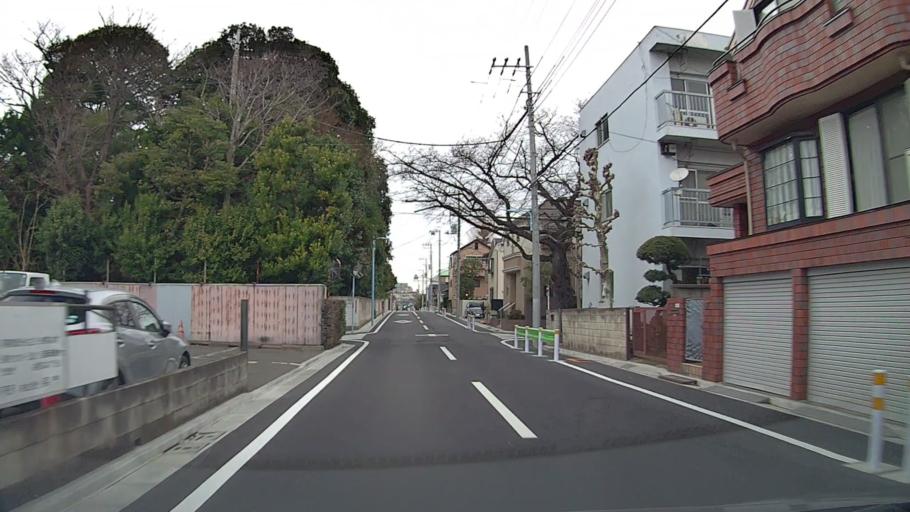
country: JP
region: Tokyo
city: Musashino
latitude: 35.7191
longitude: 139.6220
